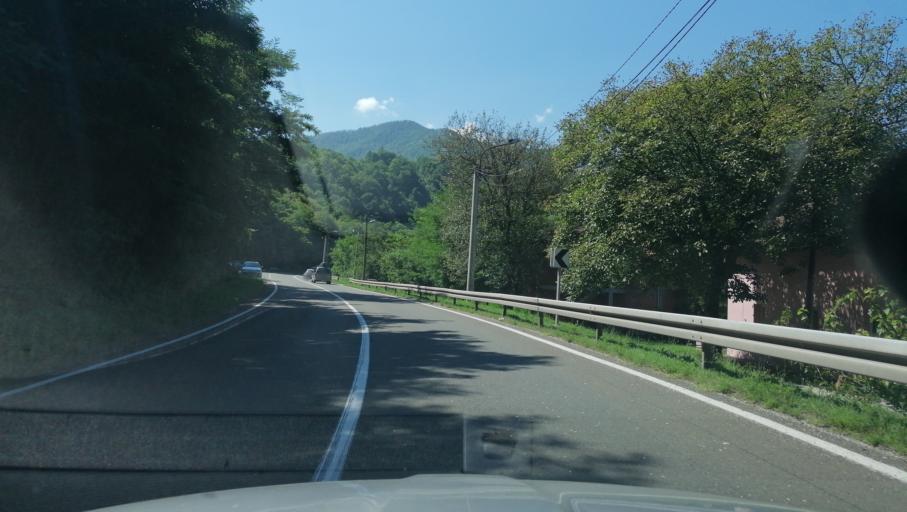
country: RS
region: Central Serbia
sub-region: Raski Okrug
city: Kraljevo
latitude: 43.6110
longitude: 20.5521
